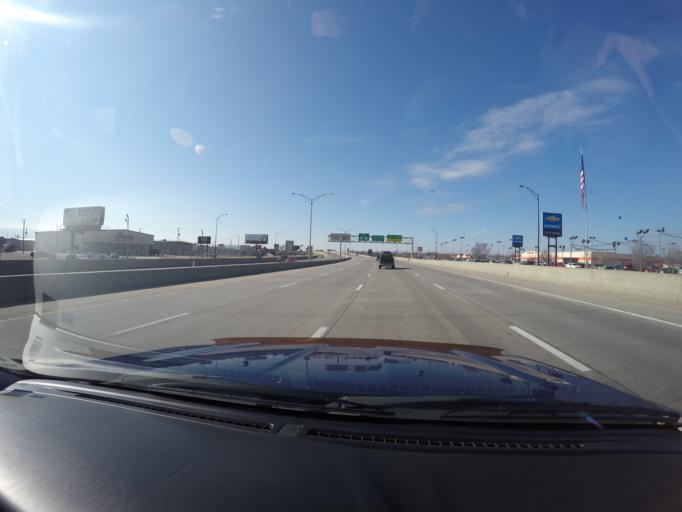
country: US
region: Kansas
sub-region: Sedgwick County
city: Wichita
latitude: 37.6724
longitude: -97.4367
